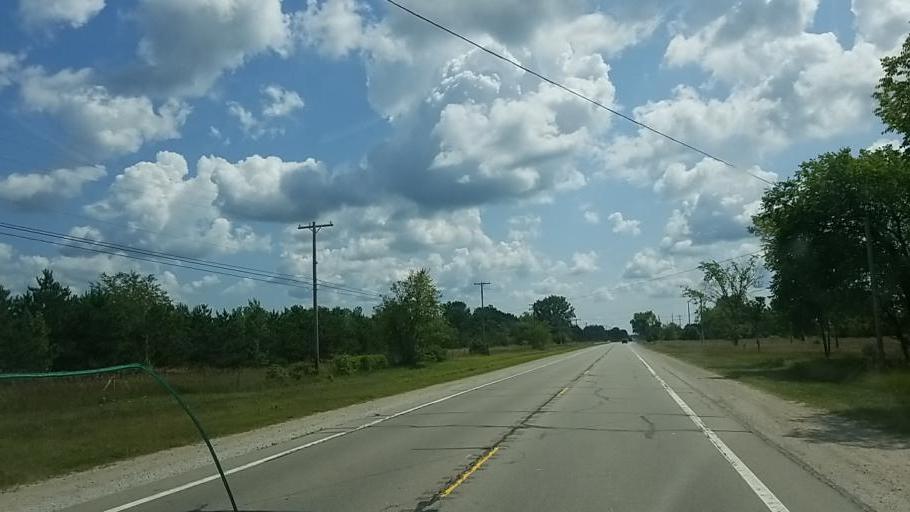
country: US
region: Michigan
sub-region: Muskegon County
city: Wolf Lake
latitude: 43.2353
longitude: -86.0307
